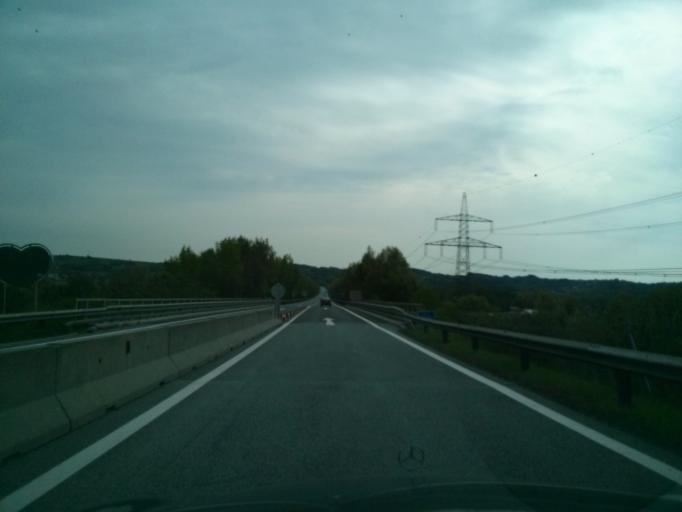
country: AT
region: Burgenland
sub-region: Politischer Bezirk Oberwart
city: Markt Allhau
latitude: 47.2802
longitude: 16.0687
